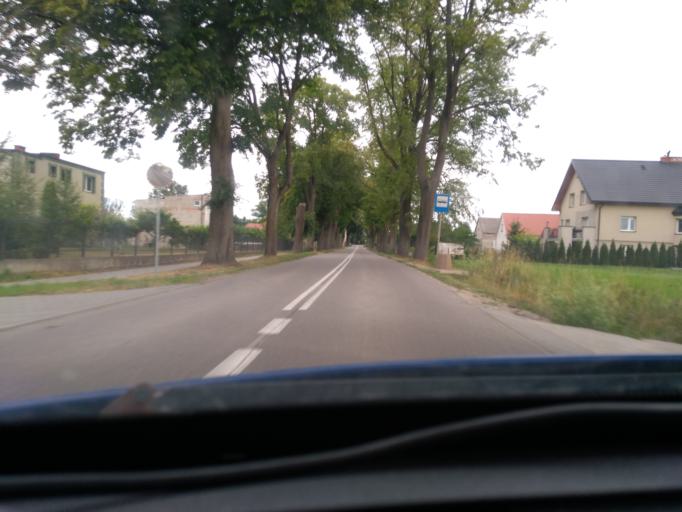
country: PL
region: Pomeranian Voivodeship
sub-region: Powiat kartuski
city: Banino
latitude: 54.3748
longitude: 18.3788
